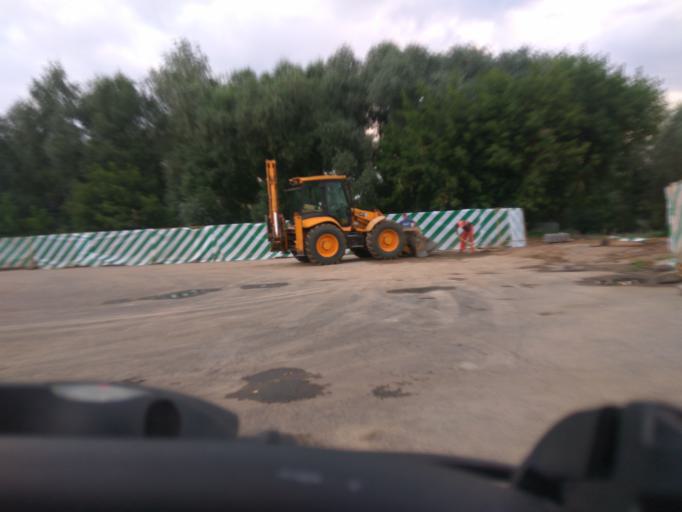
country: RU
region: Moscow
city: Brateyevo
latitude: 55.6430
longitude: 37.7757
